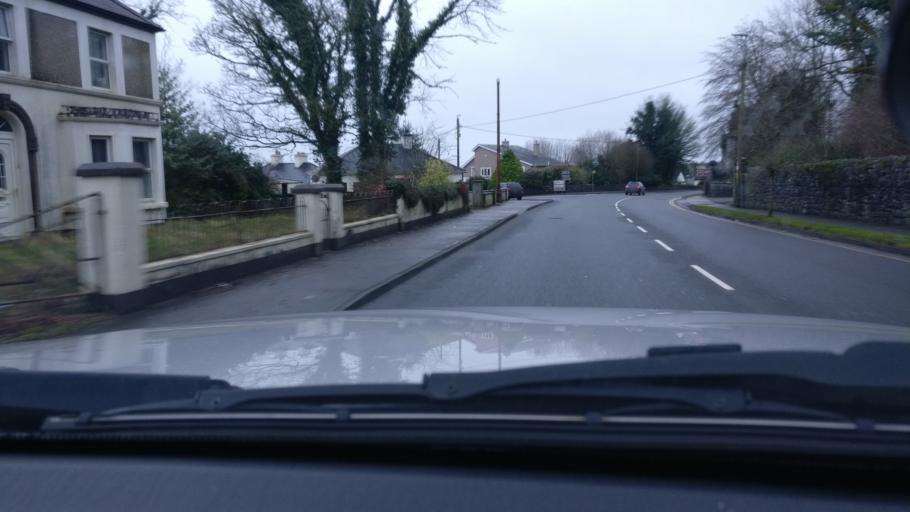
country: IE
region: Connaught
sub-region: County Galway
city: Ballinasloe
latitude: 53.3215
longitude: -8.2413
